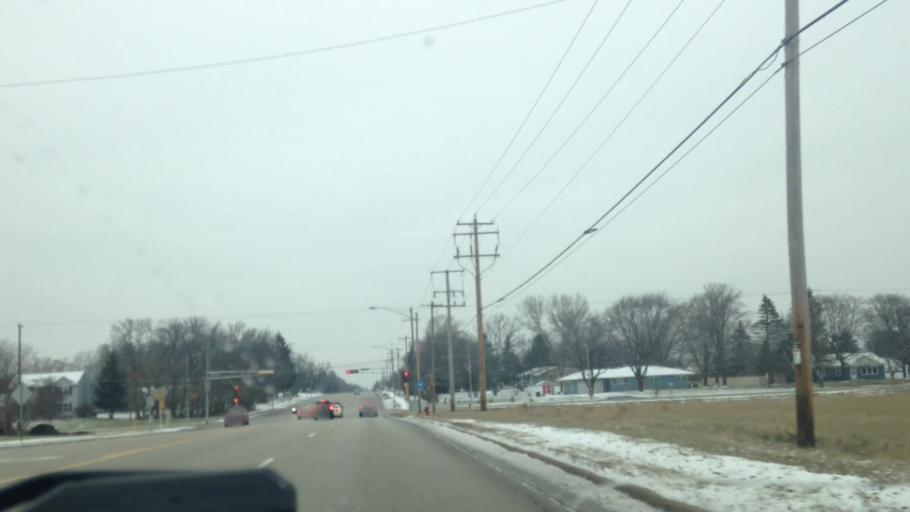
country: US
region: Wisconsin
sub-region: Waukesha County
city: Menomonee Falls
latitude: 43.1471
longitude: -88.1044
